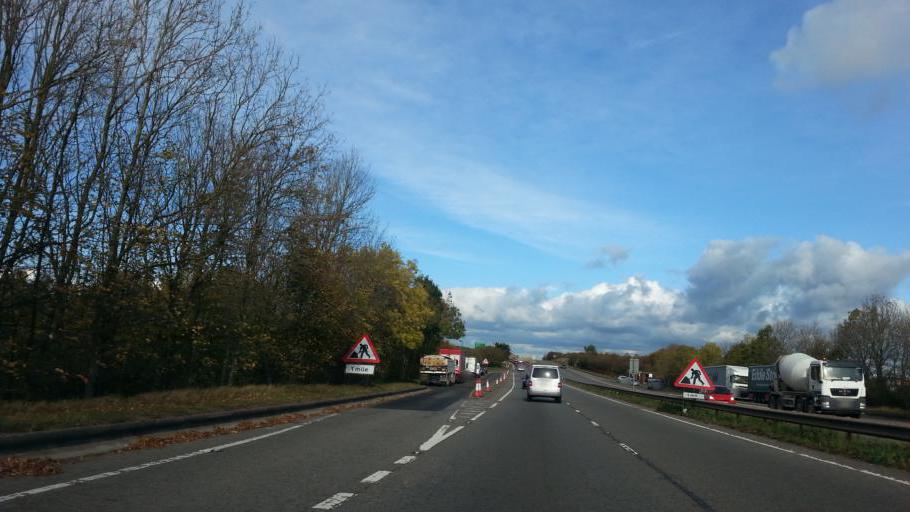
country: GB
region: England
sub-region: Leicestershire
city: Kegworth
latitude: 52.8262
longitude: -1.3036
